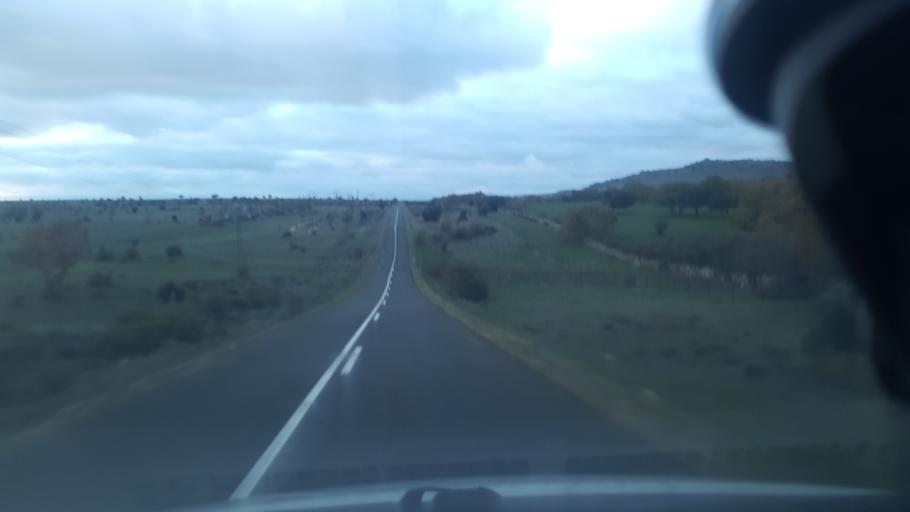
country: ES
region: Castille and Leon
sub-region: Provincia de Segovia
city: Zarzuela del Monte
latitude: 40.7057
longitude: -4.3323
